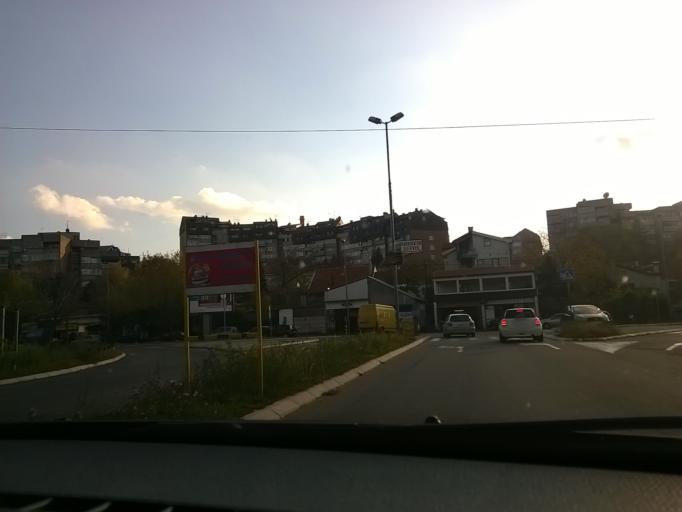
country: RS
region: Central Serbia
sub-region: Belgrade
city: Vozdovac
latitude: 44.7787
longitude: 20.4967
